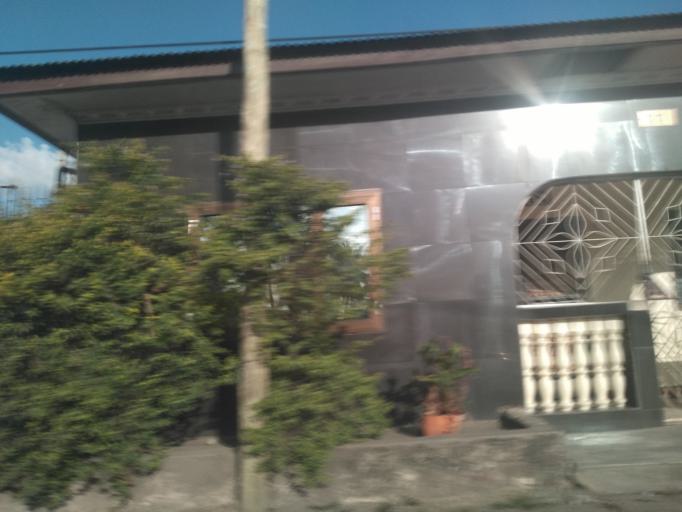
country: TZ
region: Dar es Salaam
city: Dar es Salaam
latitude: -6.8515
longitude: 39.2578
